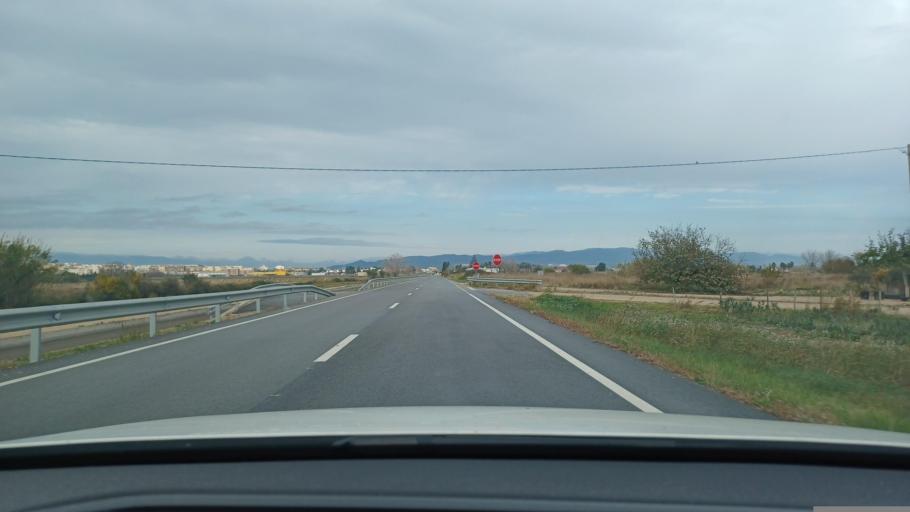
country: ES
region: Catalonia
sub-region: Provincia de Tarragona
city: Amposta
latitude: 40.6929
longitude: 0.5901
